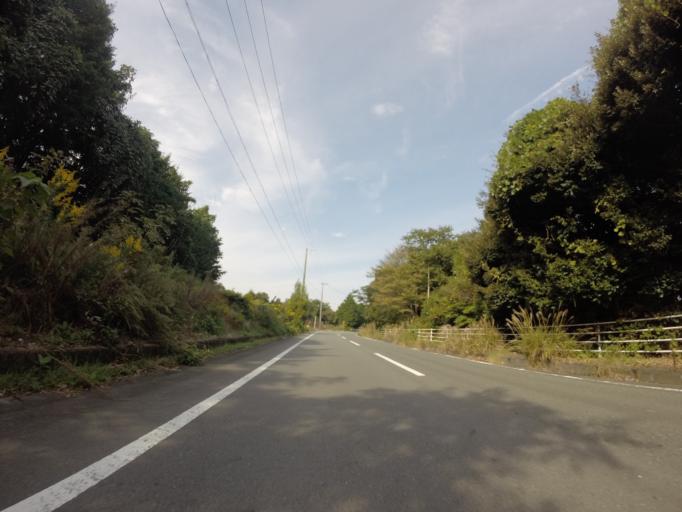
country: JP
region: Shizuoka
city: Shimada
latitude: 34.7706
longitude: 138.1663
